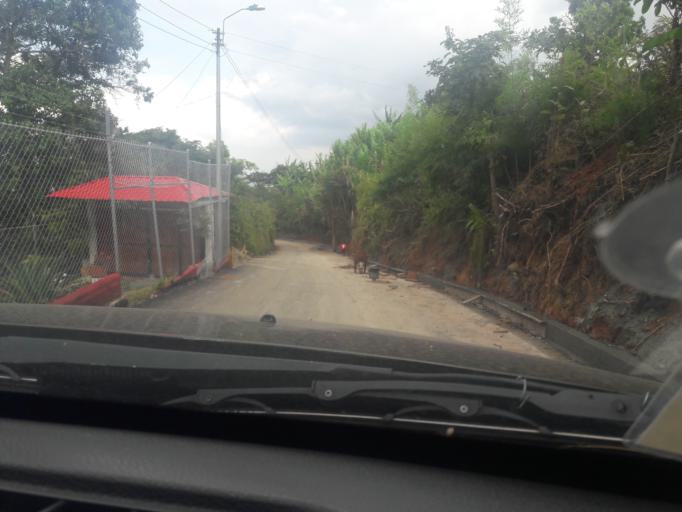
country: CO
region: Valle del Cauca
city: Cali
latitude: 3.4675
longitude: -76.6327
